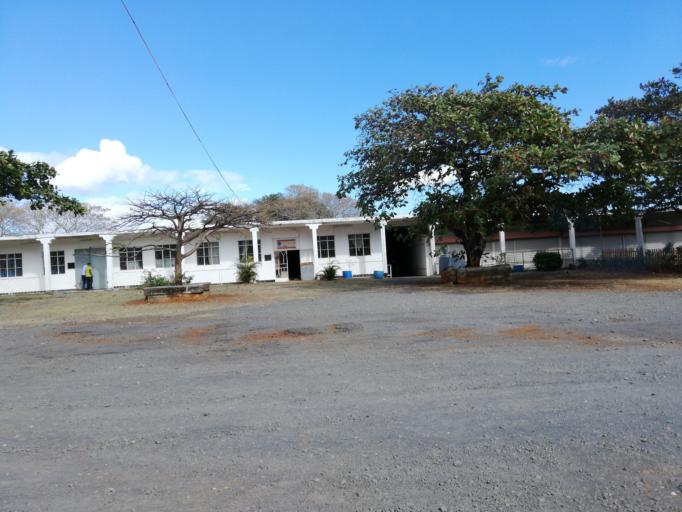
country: MU
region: Moka
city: Pailles
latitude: -20.1863
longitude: 57.4716
